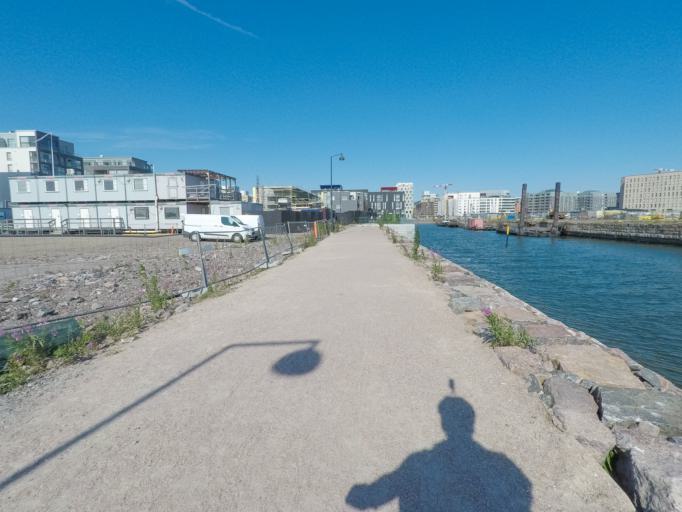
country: FI
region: Uusimaa
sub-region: Helsinki
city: Helsinki
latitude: 60.1566
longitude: 24.9050
